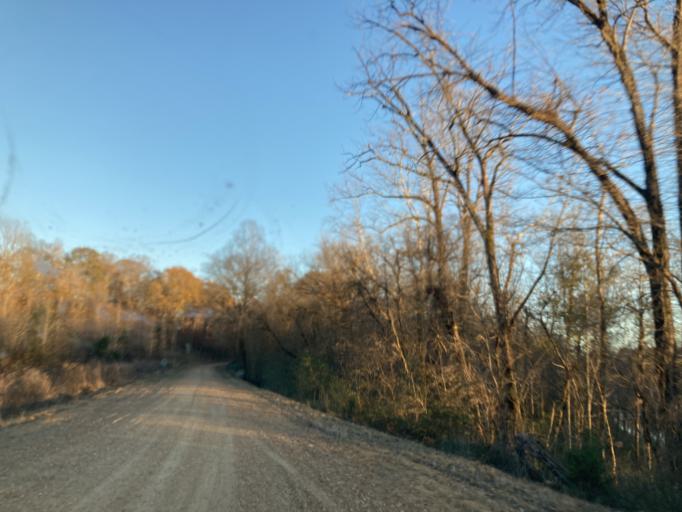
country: US
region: Mississippi
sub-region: Yazoo County
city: Yazoo City
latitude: 32.9723
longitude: -90.2650
